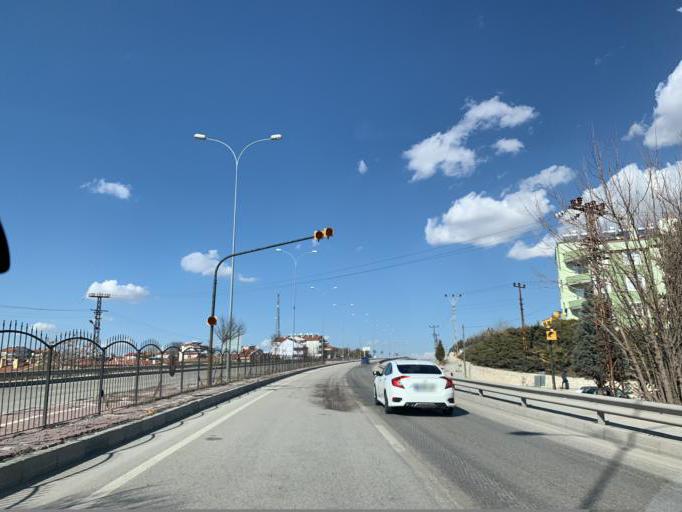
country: TR
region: Konya
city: Cihanbeyli
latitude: 38.6599
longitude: 32.9178
